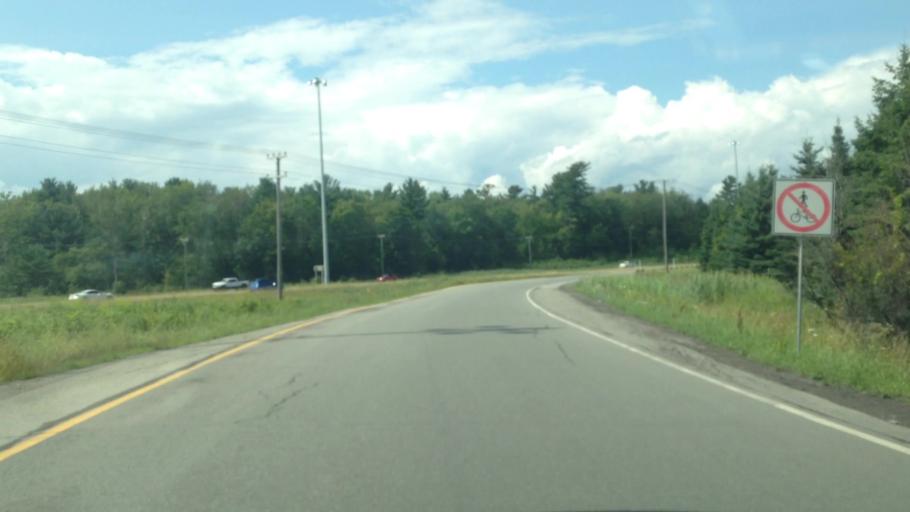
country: CA
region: Quebec
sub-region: Laurentides
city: Saint-Jerome
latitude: 45.7974
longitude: -74.0189
